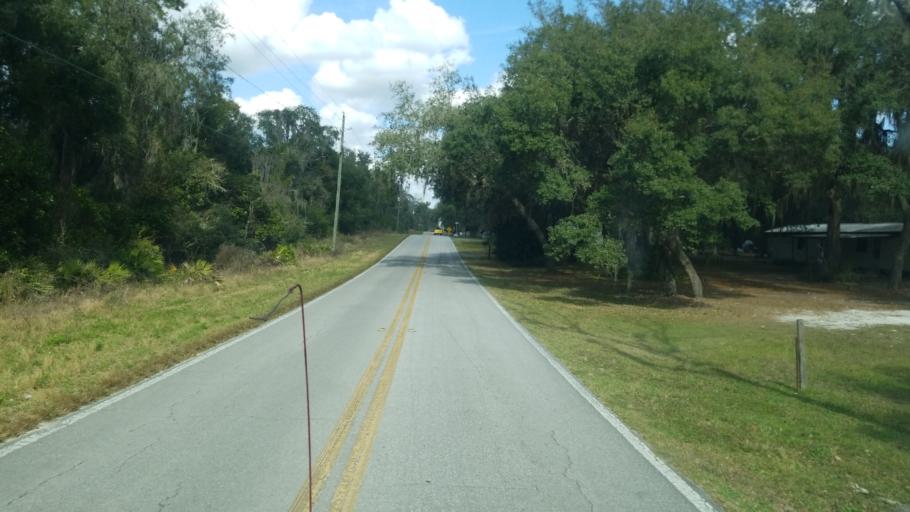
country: US
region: Florida
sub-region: Citrus County
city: Floral City
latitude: 28.7637
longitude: -82.2405
